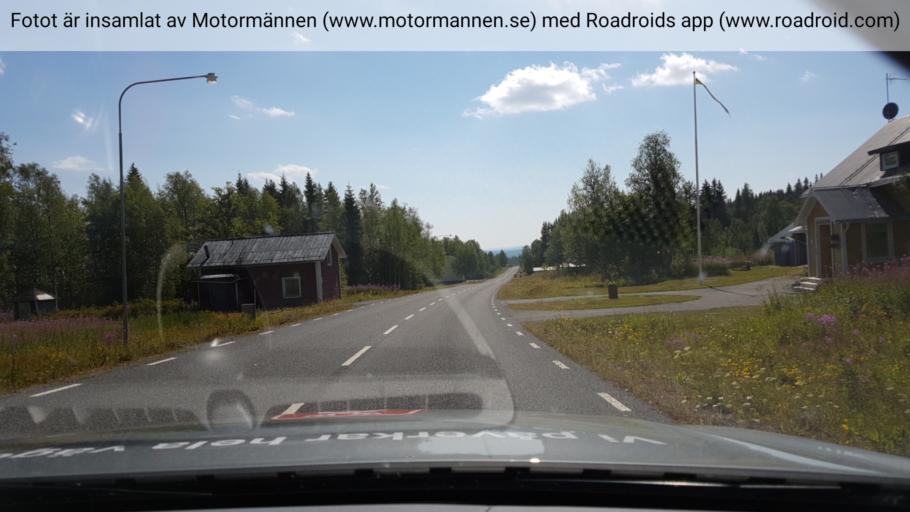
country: SE
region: Jaemtland
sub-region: OEstersunds Kommun
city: Lit
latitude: 63.3700
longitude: 15.1917
